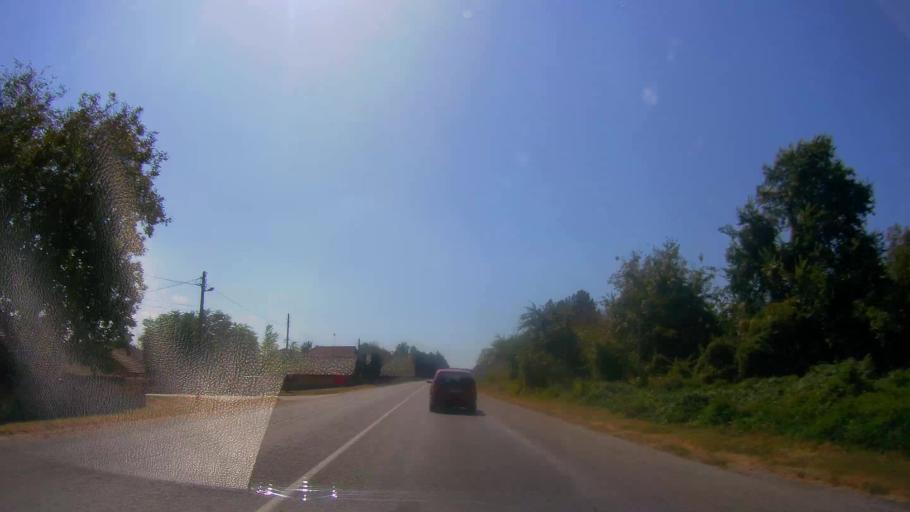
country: BG
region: Veliko Turnovo
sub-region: Obshtina Polski Trumbesh
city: Polski Trumbesh
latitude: 43.2676
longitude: 25.6436
